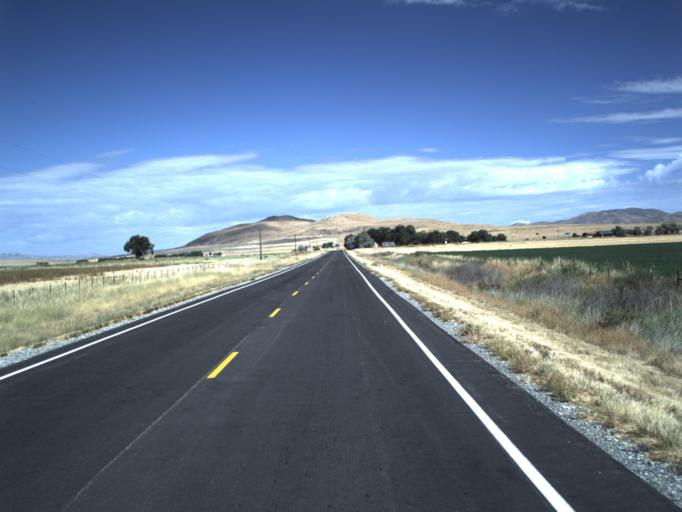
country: US
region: Utah
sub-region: Box Elder County
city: Garland
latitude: 41.7715
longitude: -112.4351
